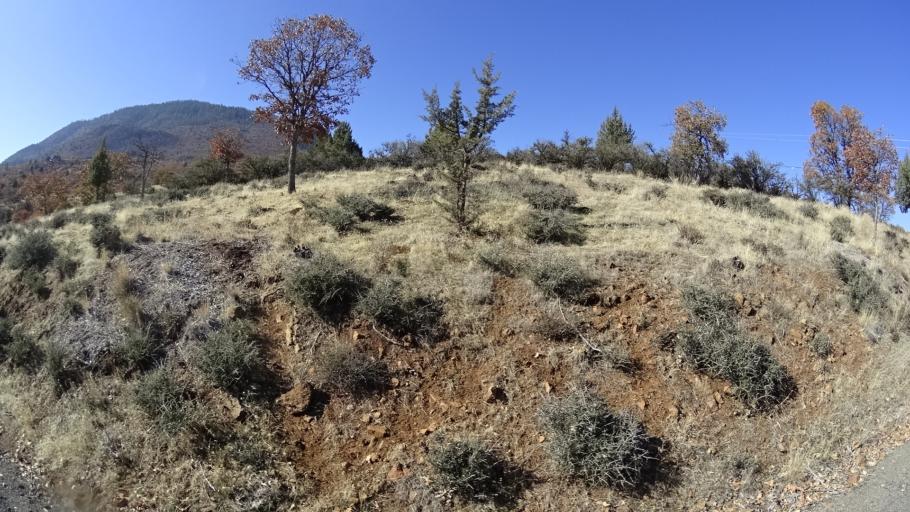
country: US
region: California
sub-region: Siskiyou County
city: Montague
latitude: 41.8758
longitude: -122.4835
